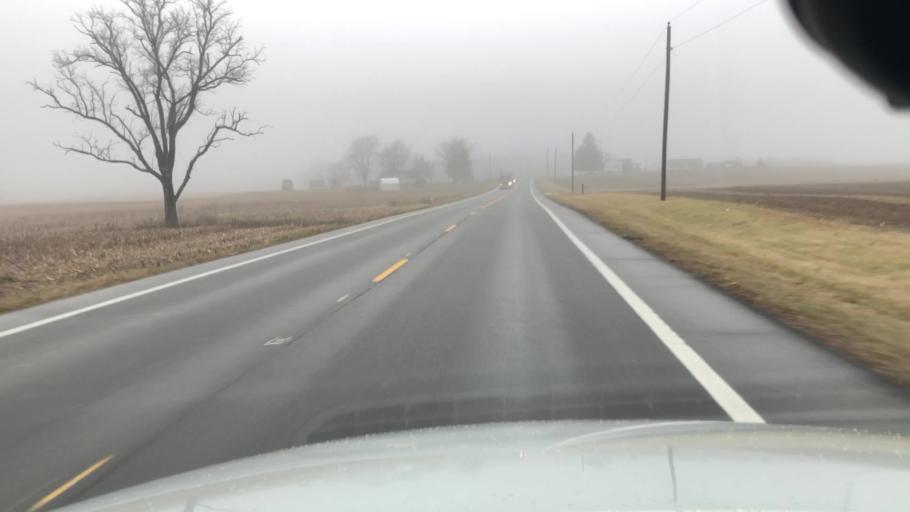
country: US
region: Ohio
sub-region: Logan County
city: Lakeview
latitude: 40.6048
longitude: -83.8843
